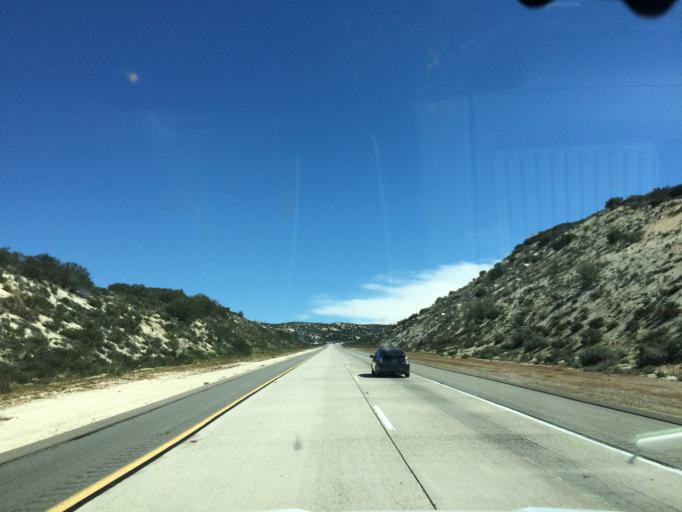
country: US
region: California
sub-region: San Diego County
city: Campo
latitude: 32.7222
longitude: -116.4001
